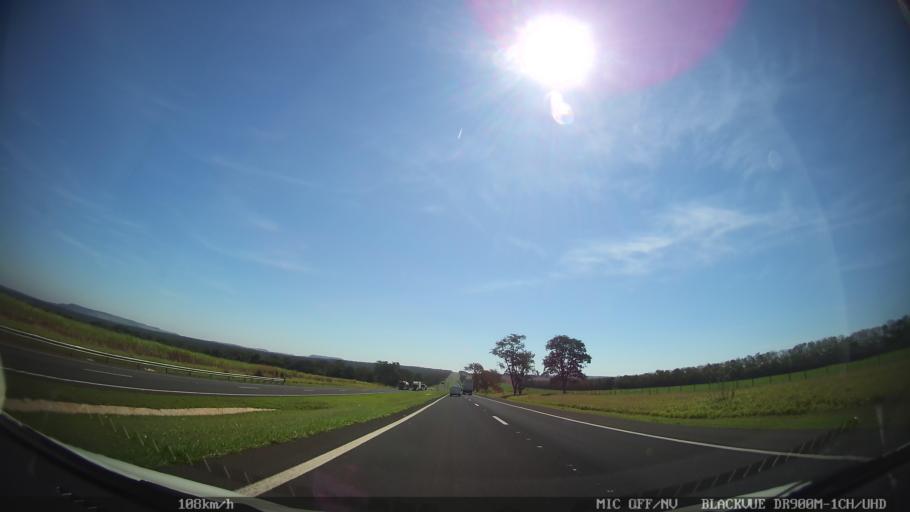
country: BR
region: Sao Paulo
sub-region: Santa Rita Do Passa Quatro
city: Santa Rita do Passa Quatro
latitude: -21.6457
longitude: -47.6110
